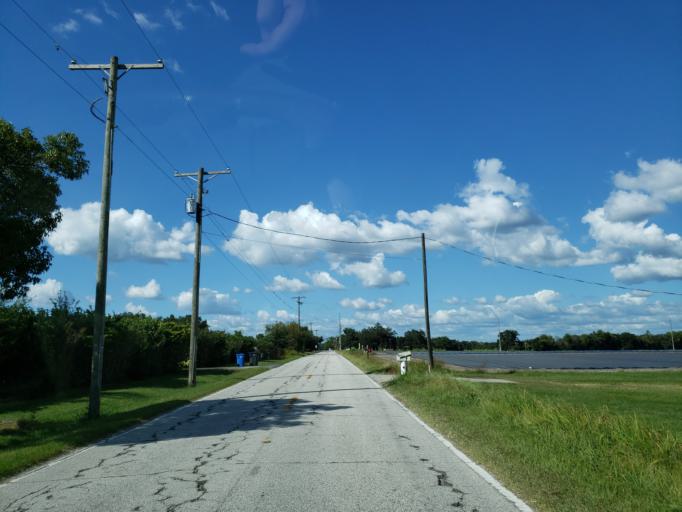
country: US
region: Florida
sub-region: Hillsborough County
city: Dover
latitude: 27.9641
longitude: -82.2031
